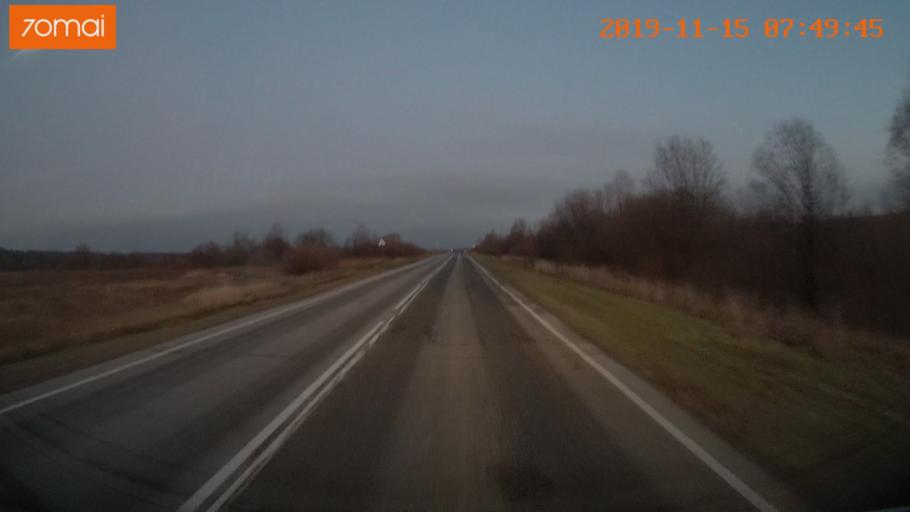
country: RU
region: Vologda
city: Cherepovets
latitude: 58.8627
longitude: 38.2277
